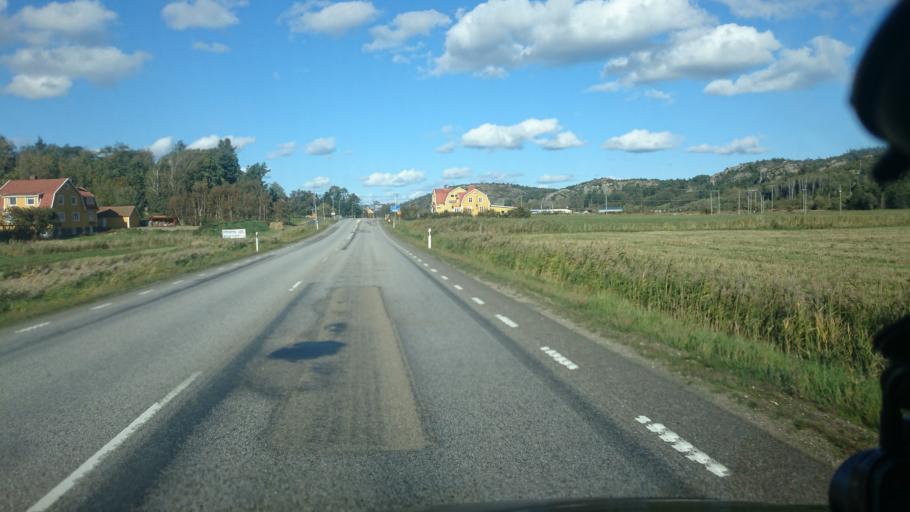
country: SE
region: Vaestra Goetaland
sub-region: Lysekils Kommun
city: Lysekil
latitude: 58.3155
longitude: 11.4846
